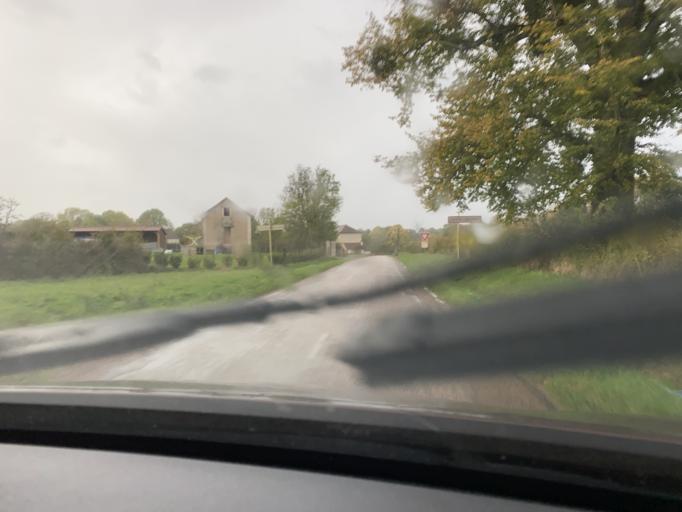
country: FR
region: Bourgogne
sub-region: Departement de la Cote-d'Or
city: Saulieu
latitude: 47.3604
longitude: 4.2537
